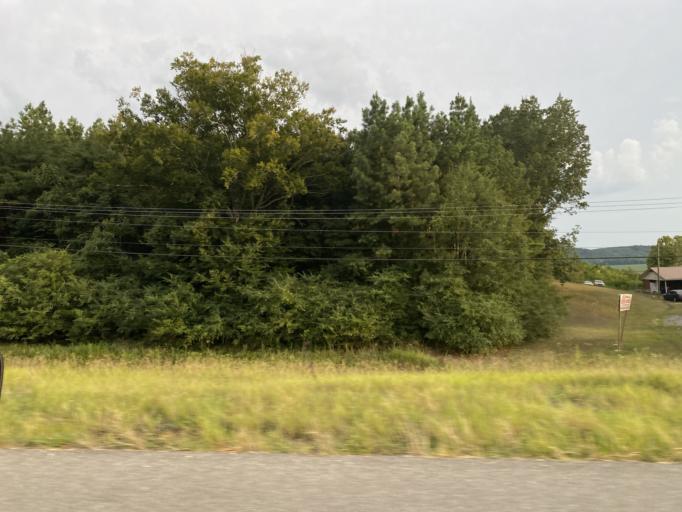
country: US
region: Alabama
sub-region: Franklin County
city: Red Bay
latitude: 34.4492
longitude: -88.0733
